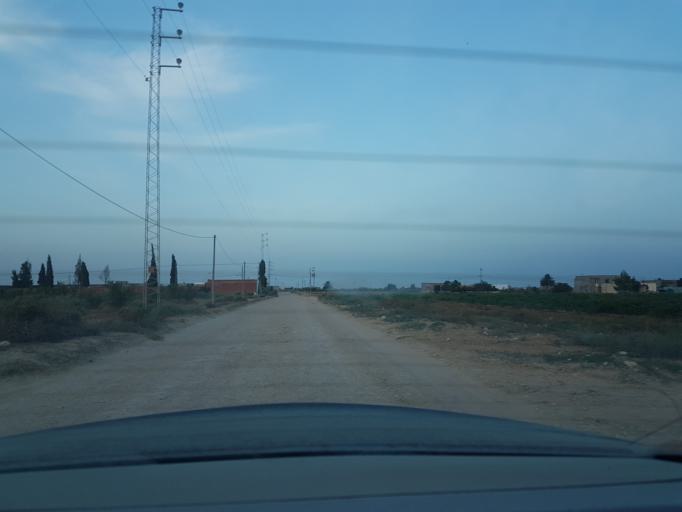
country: TN
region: Safaqis
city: Sfax
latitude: 34.7057
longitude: 10.6844
